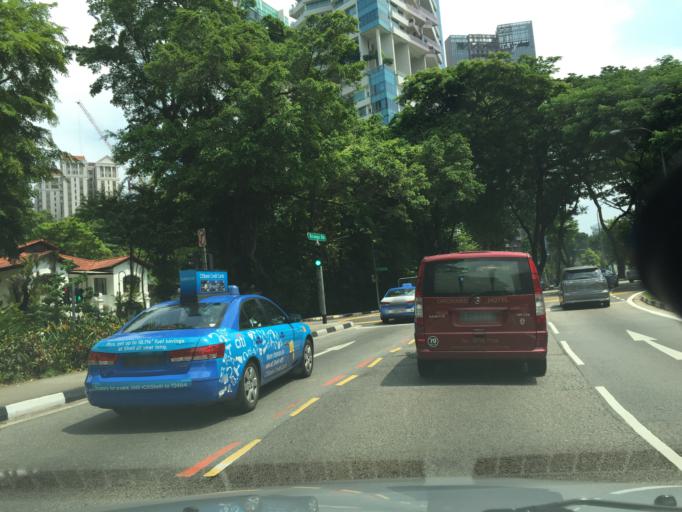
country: SG
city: Singapore
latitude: 1.3003
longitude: 103.8359
